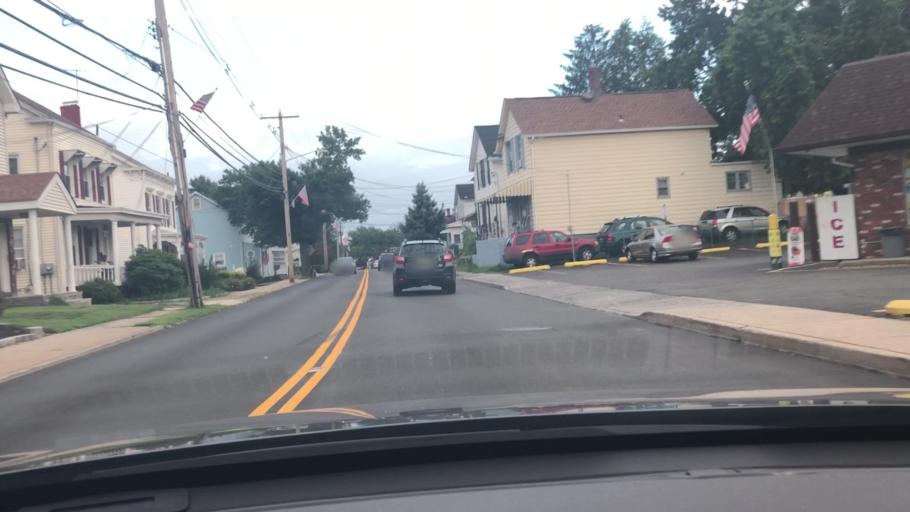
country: US
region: New Jersey
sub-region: Middlesex County
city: Milltown
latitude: 40.4468
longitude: -74.4340
